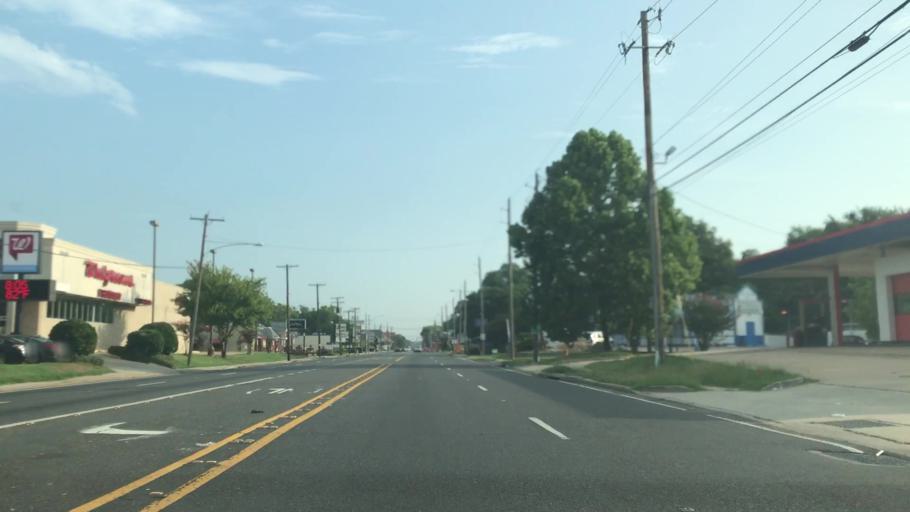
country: US
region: Louisiana
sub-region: Bossier Parish
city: Bossier City
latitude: 32.4568
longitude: -93.7221
